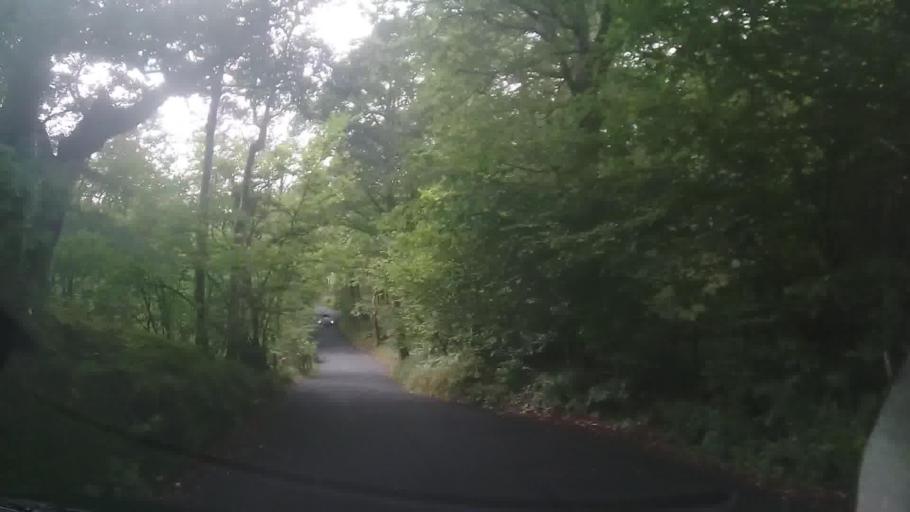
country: GB
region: England
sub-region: Cumbria
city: Ambleside
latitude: 54.4201
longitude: -3.0373
